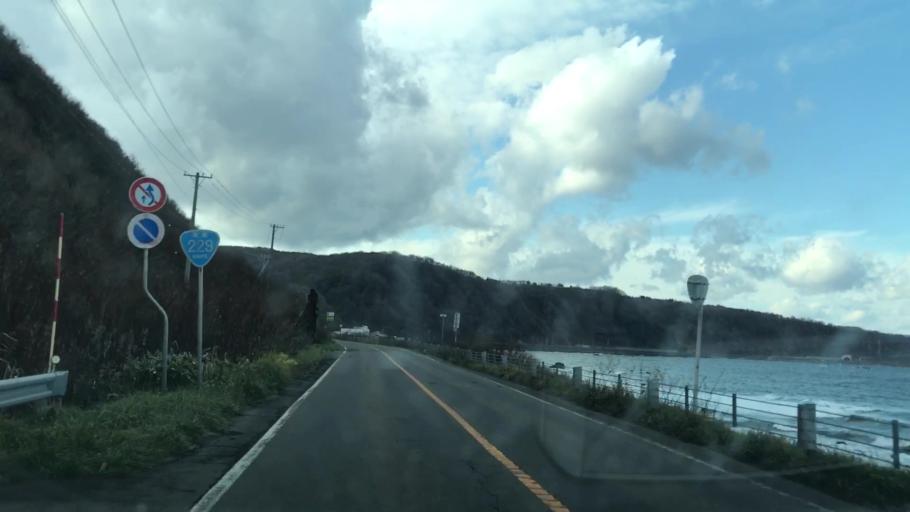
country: JP
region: Hokkaido
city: Yoichi
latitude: 43.3312
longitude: 140.4344
